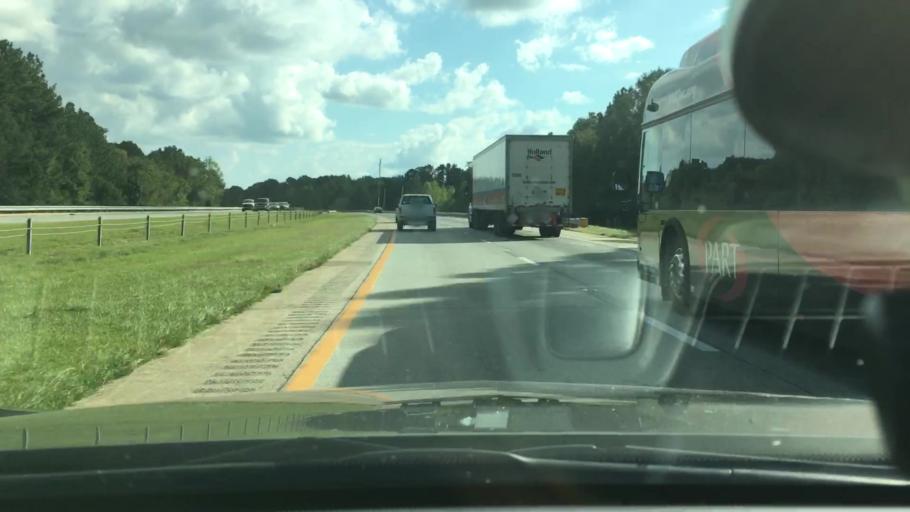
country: US
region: North Carolina
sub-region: Orange County
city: Chapel Hill
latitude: 35.9893
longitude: -79.0756
